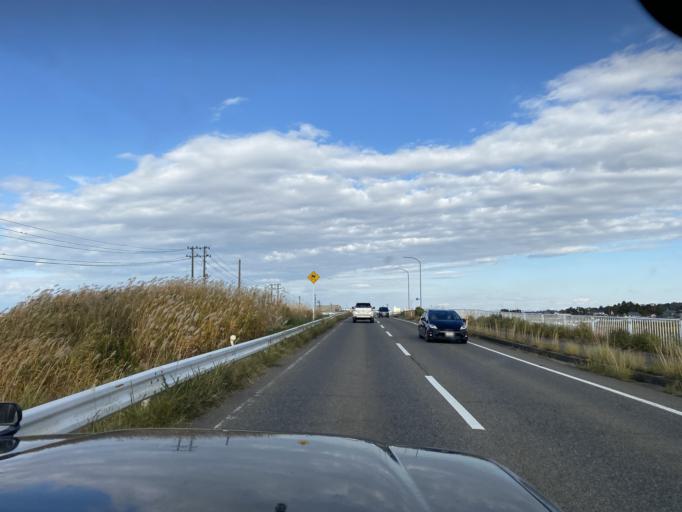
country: JP
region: Niigata
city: Niitsu-honcho
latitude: 37.7763
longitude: 139.1067
